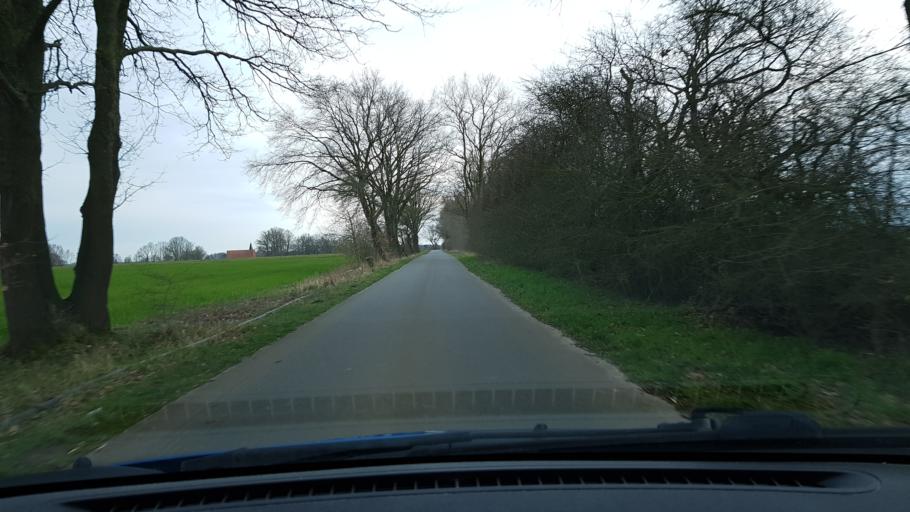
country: DE
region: Lower Saxony
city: Oetzen
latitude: 53.0109
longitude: 10.6543
